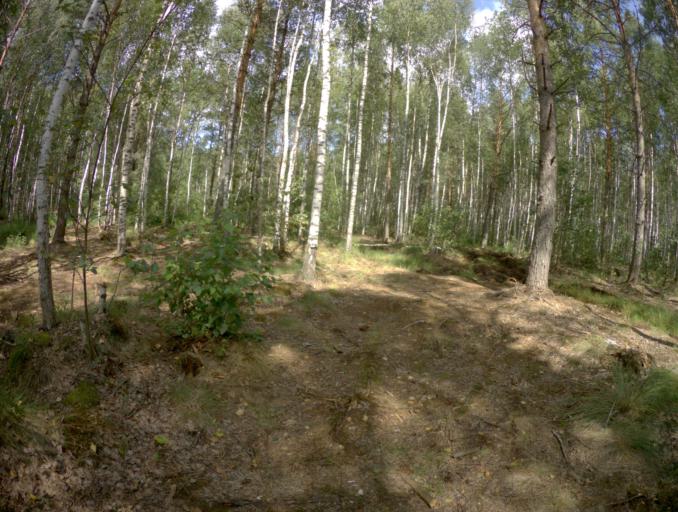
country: RU
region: Vladimir
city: Vorsha
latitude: 55.9480
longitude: 40.1935
